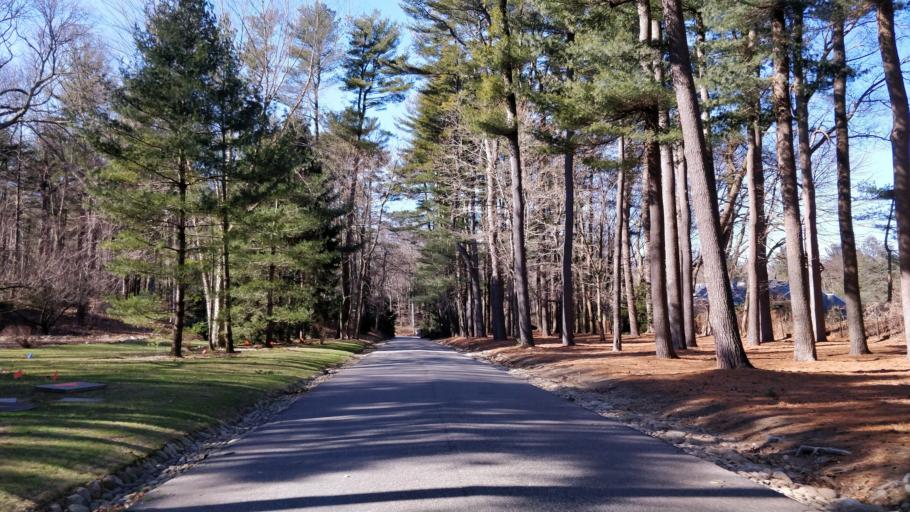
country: US
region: New York
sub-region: Nassau County
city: Brookville
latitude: 40.8214
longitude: -73.5678
